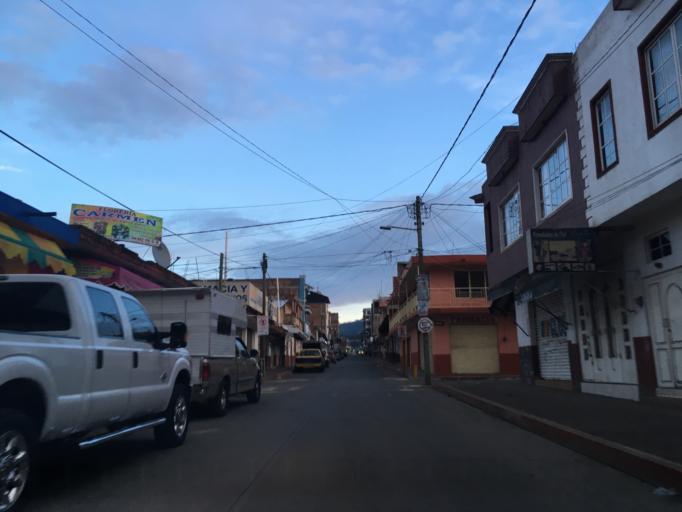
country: MX
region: Michoacan
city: Cheran
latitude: 19.6859
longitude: -101.9550
